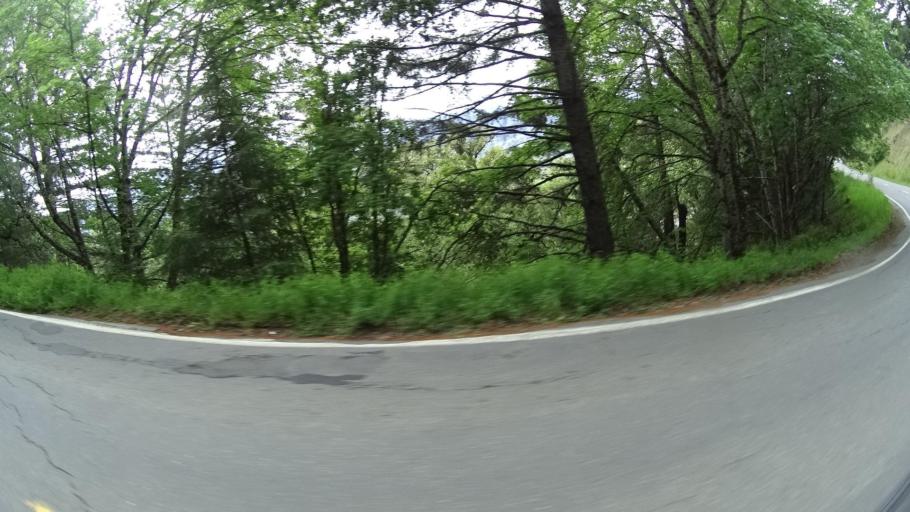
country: US
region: California
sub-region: Humboldt County
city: Redway
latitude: 40.1105
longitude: -123.7676
